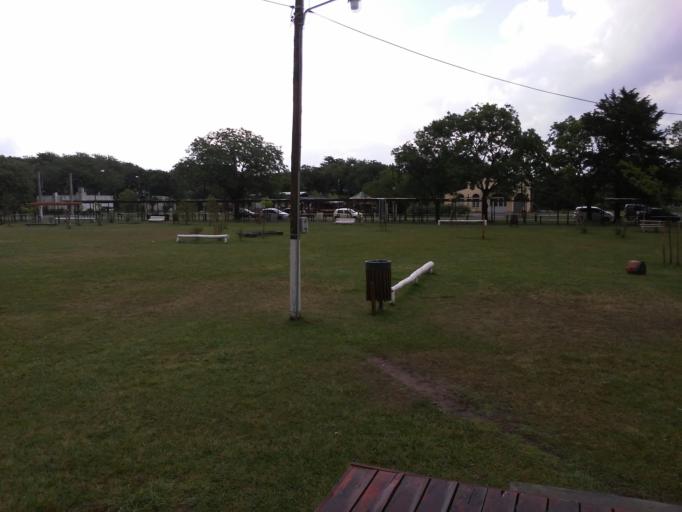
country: AR
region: Buenos Aires
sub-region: Partido de Mercedes
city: Mercedes
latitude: -34.7004
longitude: -59.3180
